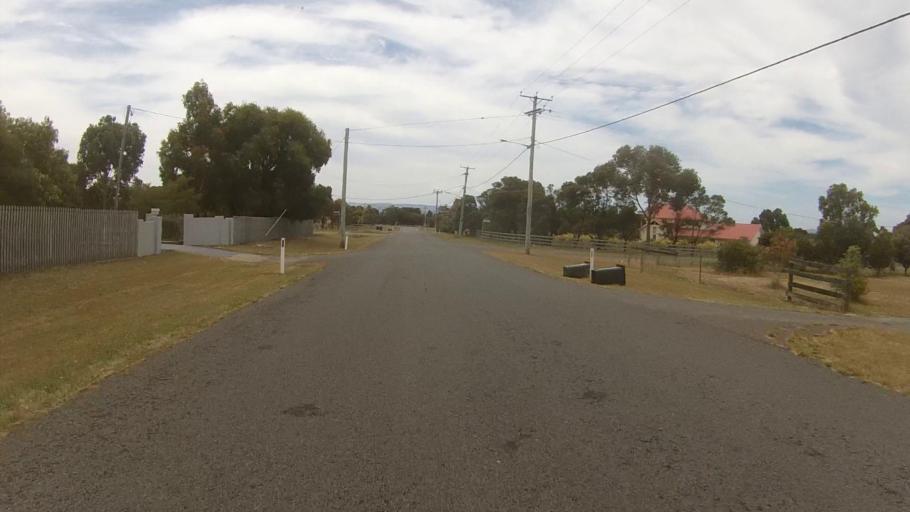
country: AU
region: Tasmania
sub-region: Clarence
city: Cambridge
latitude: -42.8456
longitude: 147.4728
